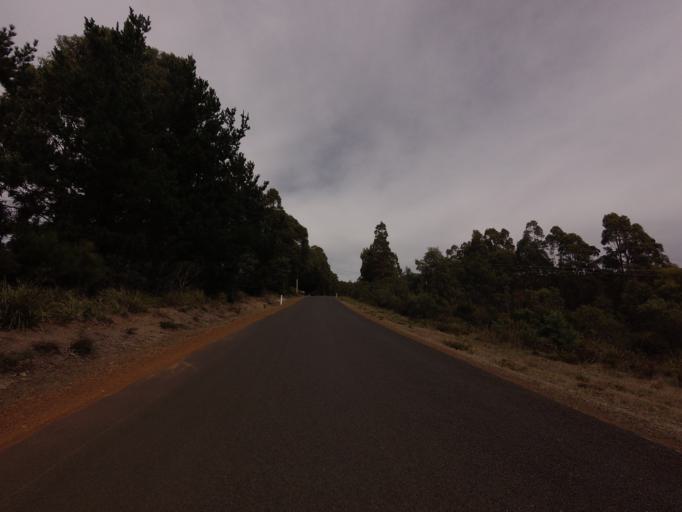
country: AU
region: Tasmania
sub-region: Sorell
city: Sorell
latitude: -42.5672
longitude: 147.5717
